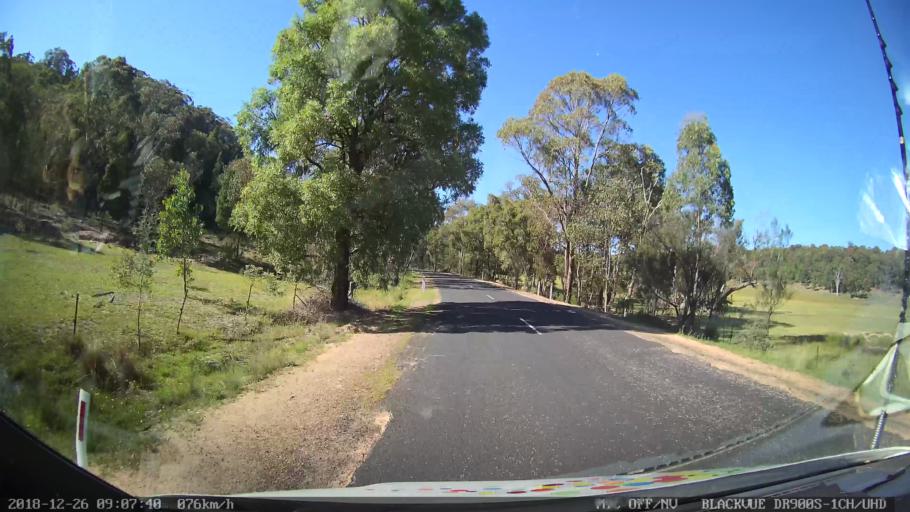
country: AU
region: New South Wales
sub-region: Mid-Western Regional
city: Kandos
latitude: -32.7080
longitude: 150.0034
